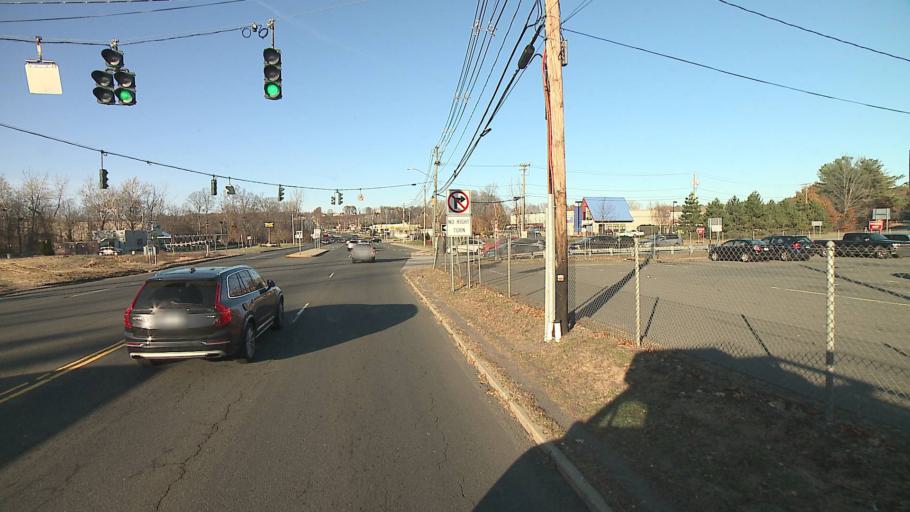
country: US
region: Connecticut
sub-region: New Haven County
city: Wallingford
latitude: 41.4924
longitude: -72.8094
